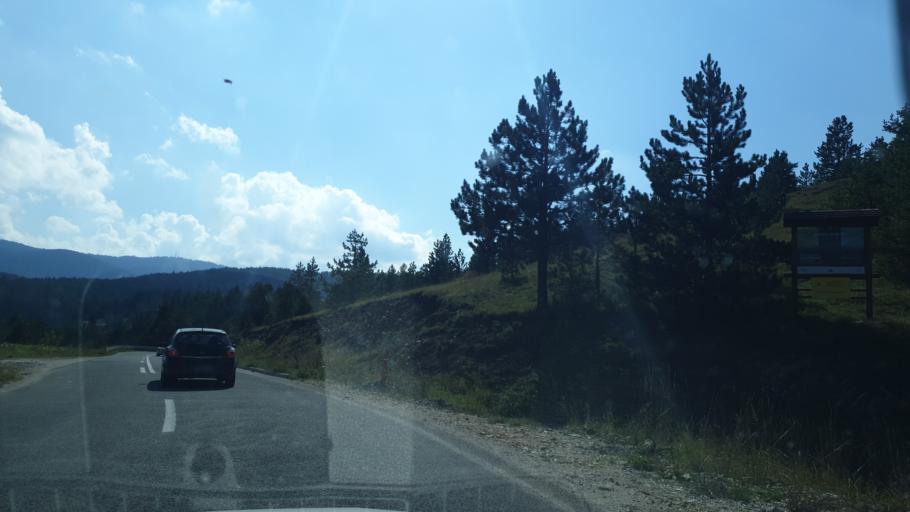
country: RS
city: Zlatibor
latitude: 43.6959
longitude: 19.6645
